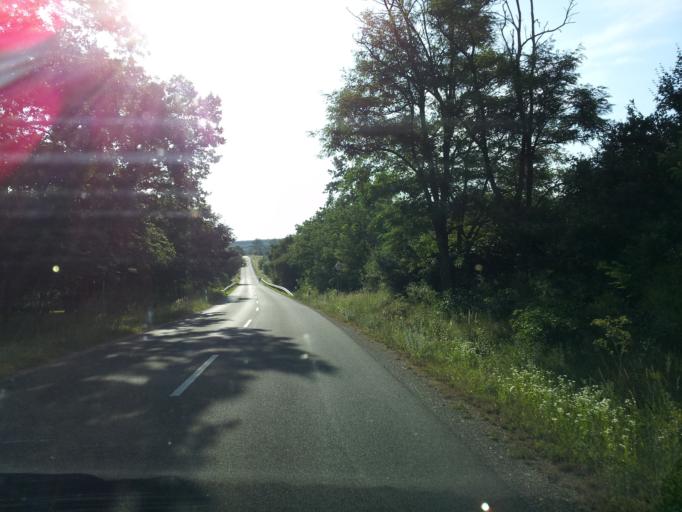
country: HU
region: Veszprem
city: Urkut
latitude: 47.0016
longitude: 17.6441
